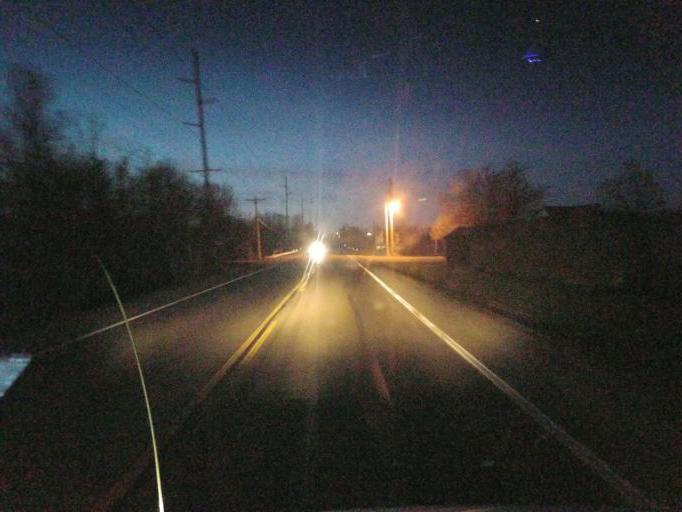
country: US
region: Ohio
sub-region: Logan County
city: Bellefontaine
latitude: 40.3944
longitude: -83.7500
